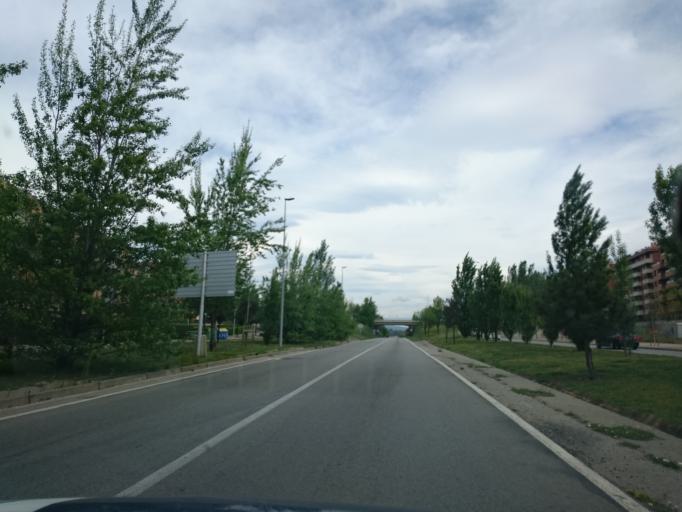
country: ES
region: Catalonia
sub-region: Provincia de Barcelona
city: Vic
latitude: 41.9316
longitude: 2.2444
